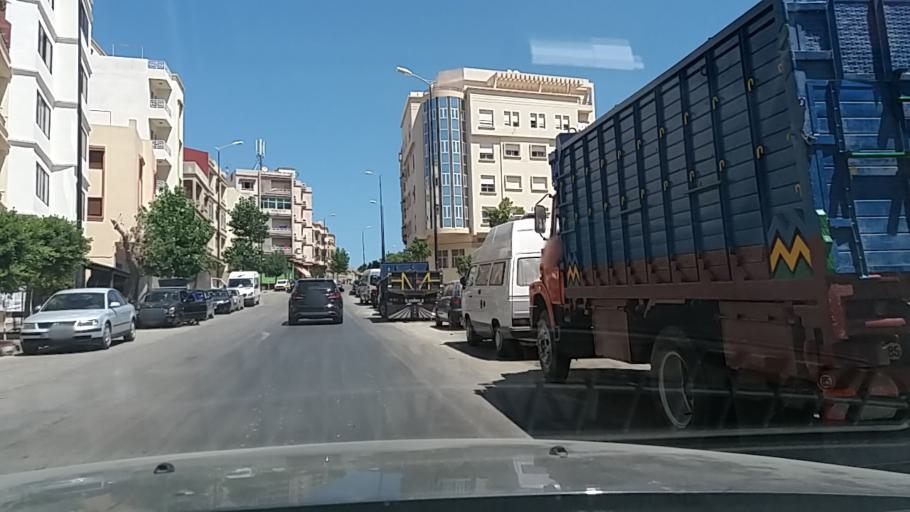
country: MA
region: Tanger-Tetouan
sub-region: Tanger-Assilah
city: Tangier
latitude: 35.7655
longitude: -5.7942
